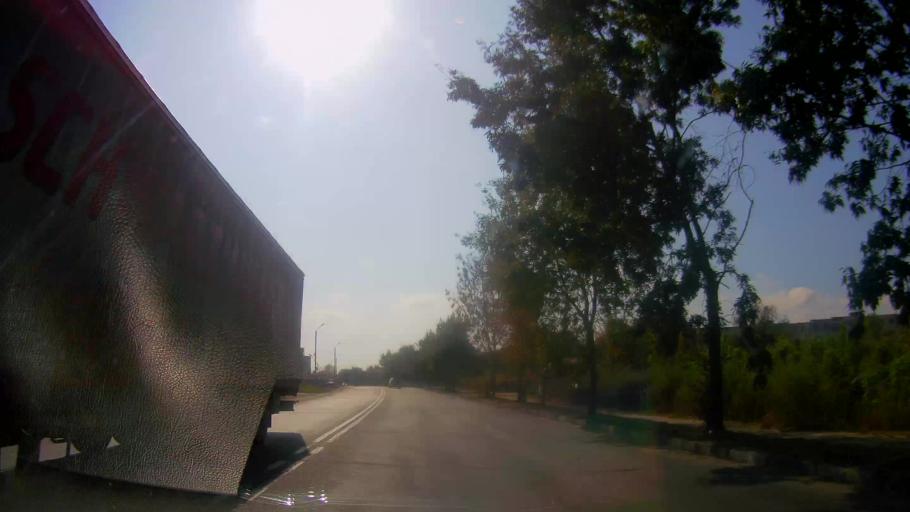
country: RO
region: Giurgiu
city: Giurgiu
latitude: 43.9128
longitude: 25.9740
